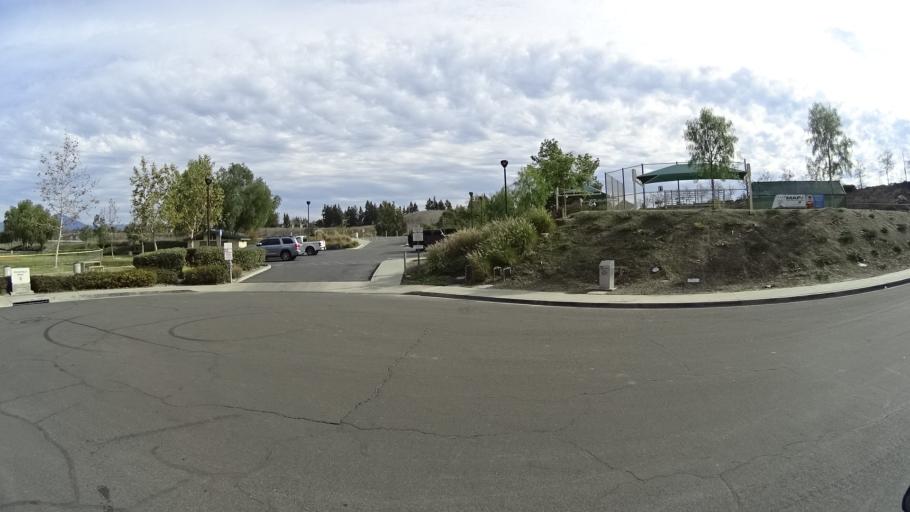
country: US
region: California
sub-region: Orange County
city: Aliso Viejo
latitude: 33.5734
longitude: -117.7179
